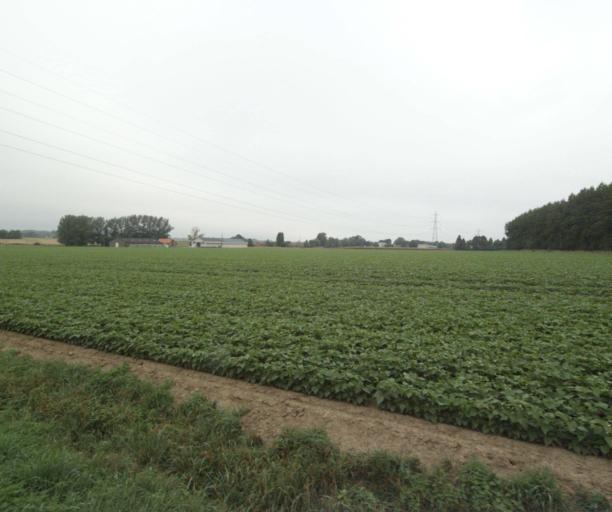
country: FR
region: Nord-Pas-de-Calais
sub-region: Departement du Nord
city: Willems
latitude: 50.6390
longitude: 3.2380
